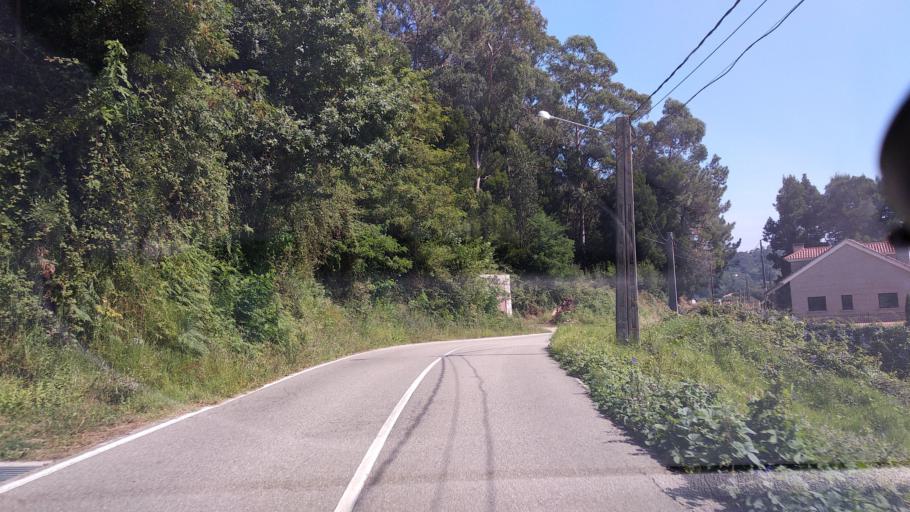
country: ES
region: Galicia
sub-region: Provincia de Pontevedra
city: Moana
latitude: 42.2789
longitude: -8.7668
